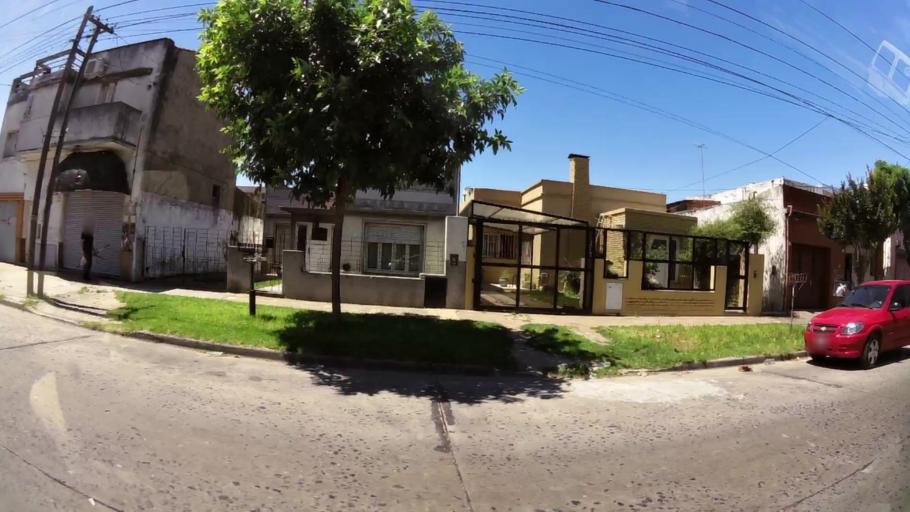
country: AR
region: Buenos Aires
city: Caseros
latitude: -34.5791
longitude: -58.5514
